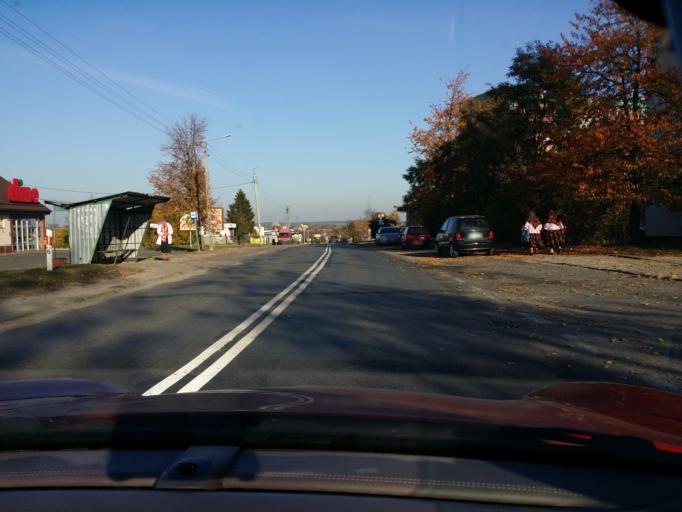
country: PL
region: Masovian Voivodeship
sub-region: Powiat radomski
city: Wierzbica
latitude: 51.2490
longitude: 21.0670
